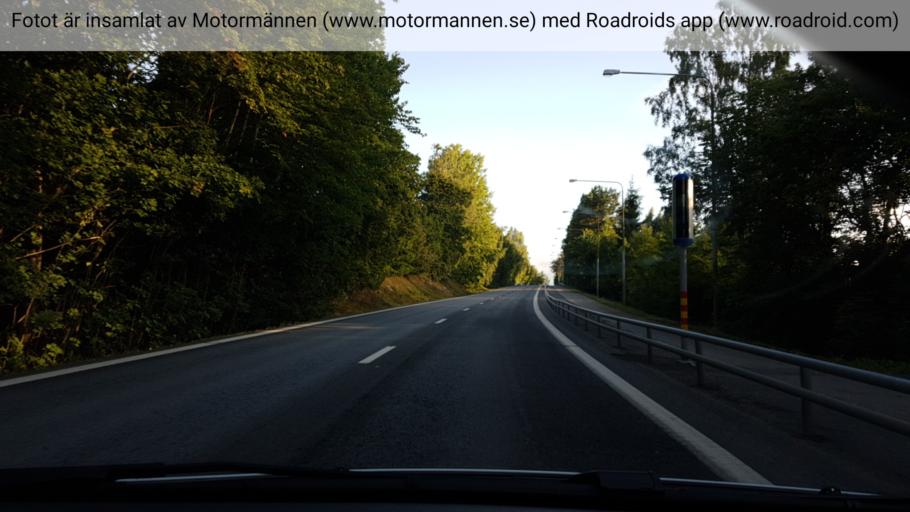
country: SE
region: Stockholm
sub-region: Tyreso Kommun
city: Bollmora
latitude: 59.2179
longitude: 18.2041
